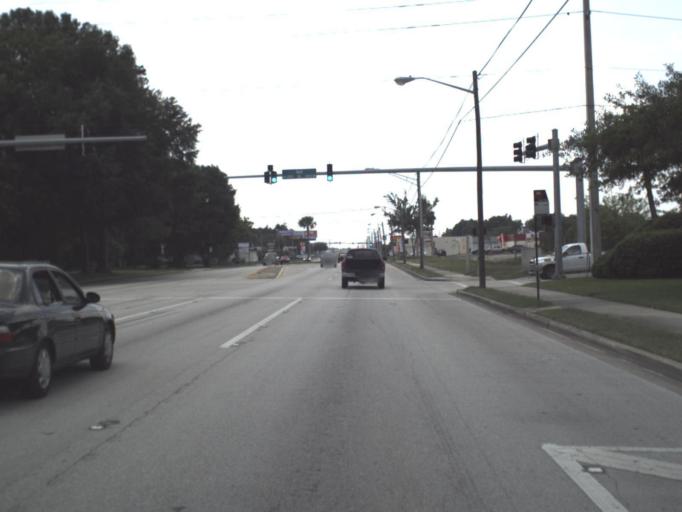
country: US
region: Florida
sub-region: Duval County
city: Jacksonville
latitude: 30.3407
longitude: -81.7312
